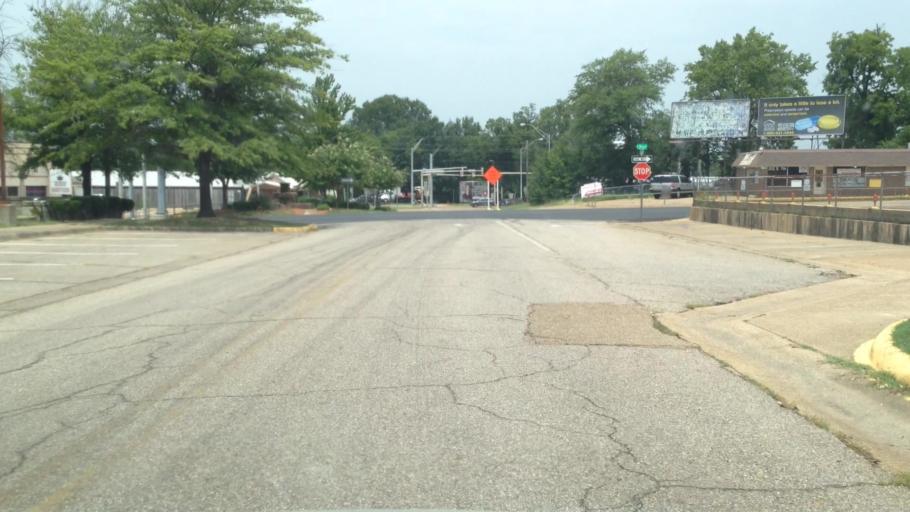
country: US
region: Texas
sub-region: Bowie County
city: Texarkana
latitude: 33.4269
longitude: -94.0424
